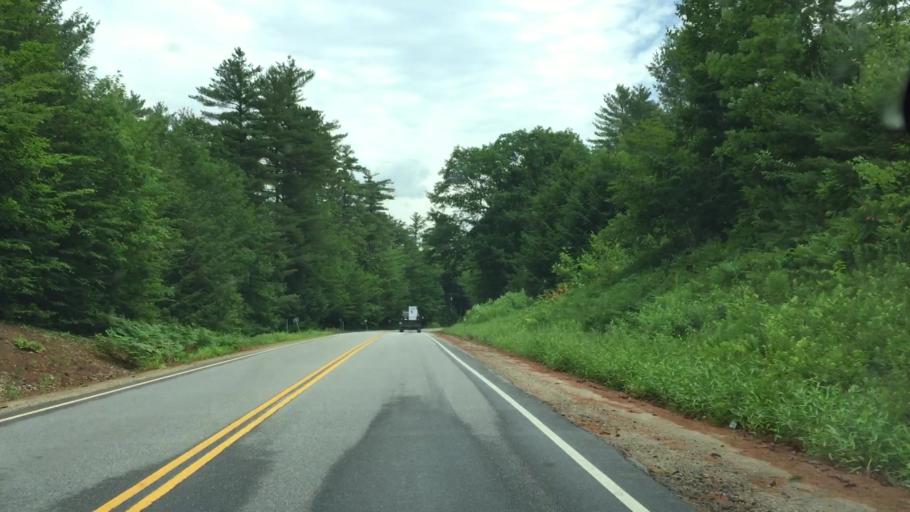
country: US
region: New Hampshire
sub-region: Carroll County
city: Sandwich
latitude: 43.7815
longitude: -71.4723
